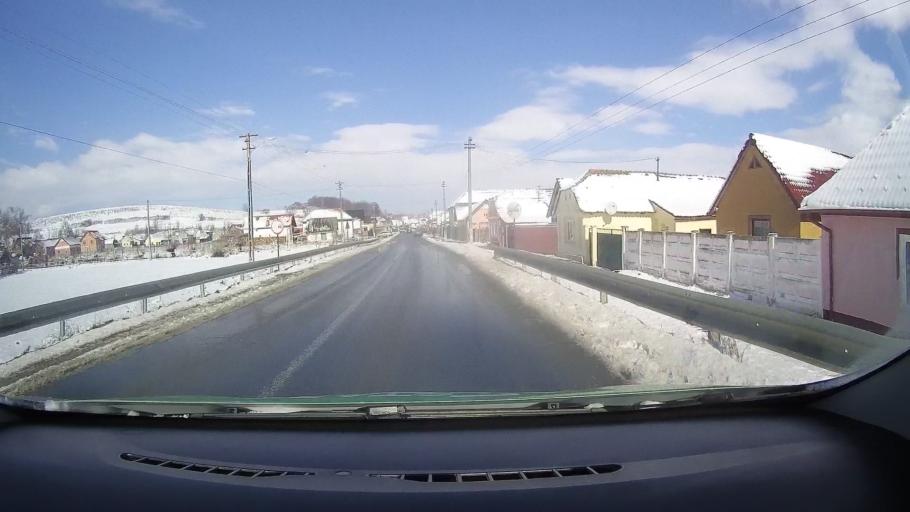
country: RO
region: Sibiu
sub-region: Comuna Nocrich
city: Nocrich
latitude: 45.8865
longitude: 24.4515
